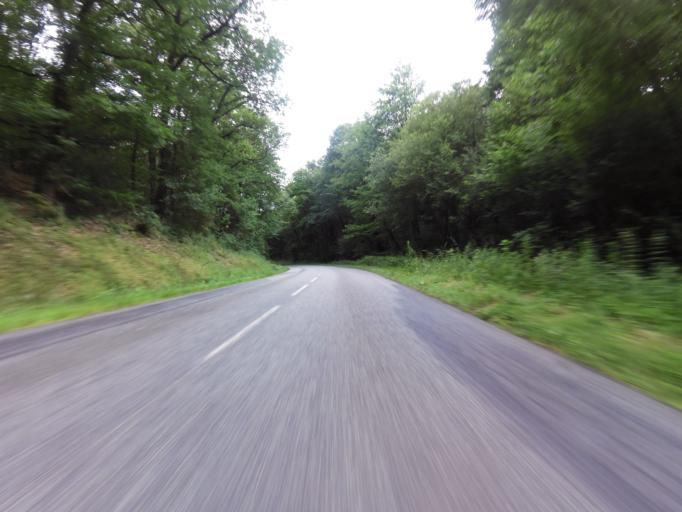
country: FR
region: Brittany
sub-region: Departement du Morbihan
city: Pluherlin
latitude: 47.7204
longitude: -2.3243
